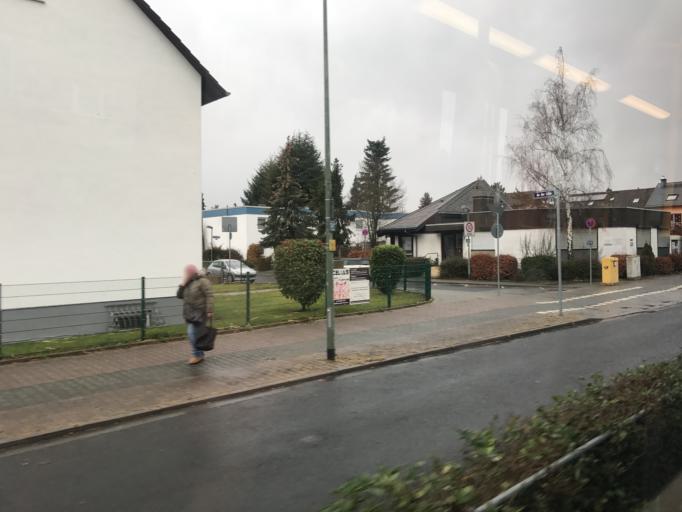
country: DE
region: Hesse
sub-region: Regierungsbezirk Darmstadt
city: Eschborn
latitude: 50.1373
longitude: 8.6246
